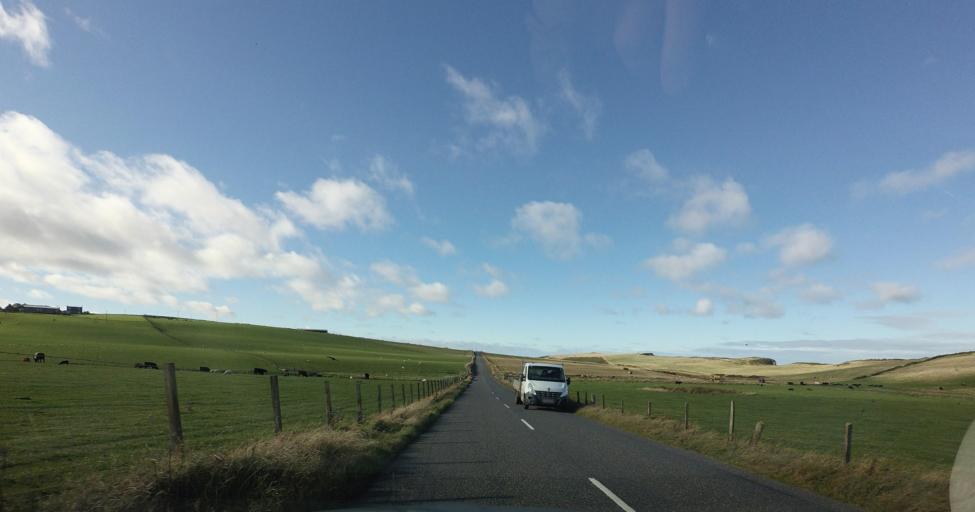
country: GB
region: Scotland
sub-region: Aberdeenshire
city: Macduff
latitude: 57.6641
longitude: -2.3922
